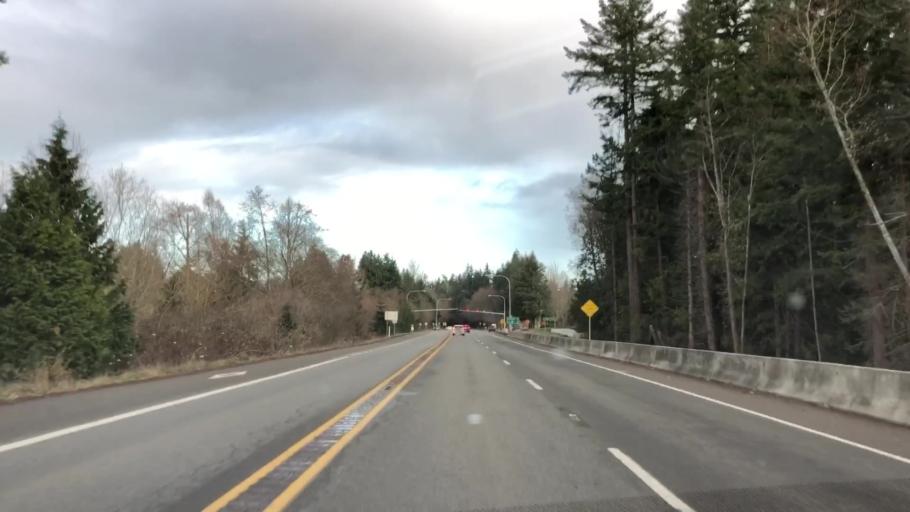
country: US
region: Washington
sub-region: Kitsap County
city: Bainbridge Island
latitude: 47.6334
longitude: -122.5159
